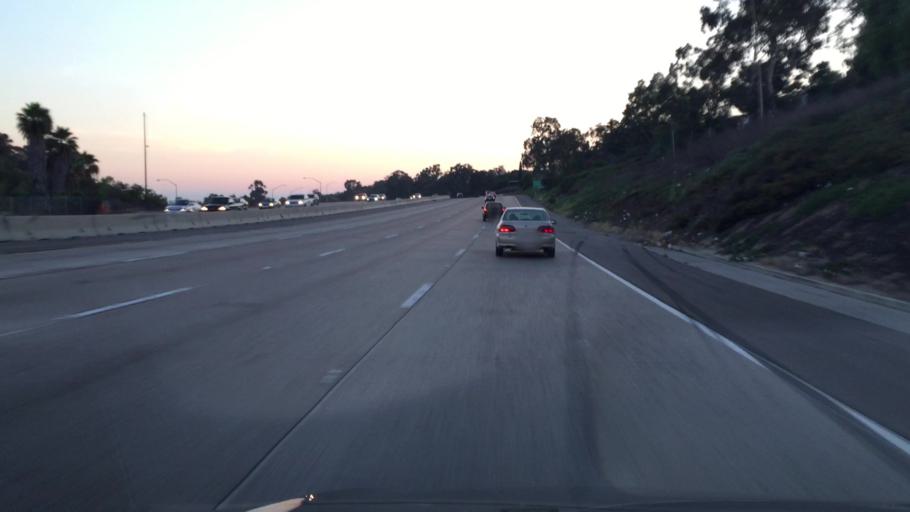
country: US
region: California
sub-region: San Diego County
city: Lemon Grove
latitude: 32.7285
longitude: -117.0683
